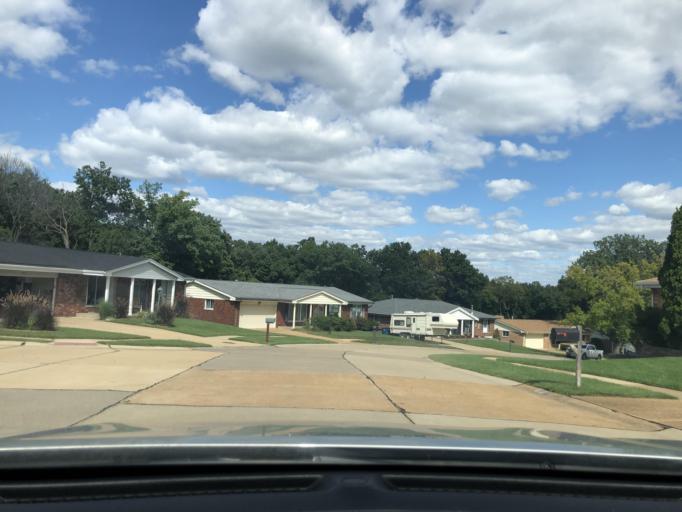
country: US
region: Missouri
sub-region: Saint Louis County
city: Concord
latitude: 38.5022
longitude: -90.3561
